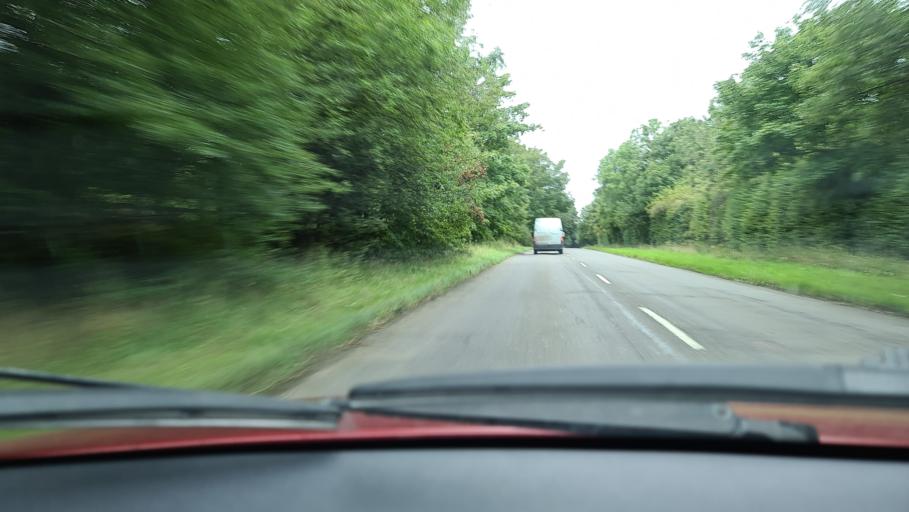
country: GB
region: England
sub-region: Buckinghamshire
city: Great Missenden
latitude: 51.7032
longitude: -0.6569
